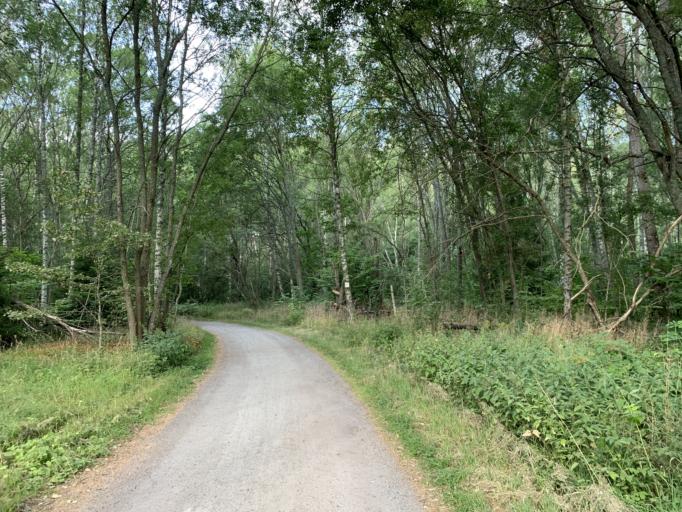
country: SE
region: Stockholm
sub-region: Solna Kommun
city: Rasunda
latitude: 59.3945
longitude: 17.9745
